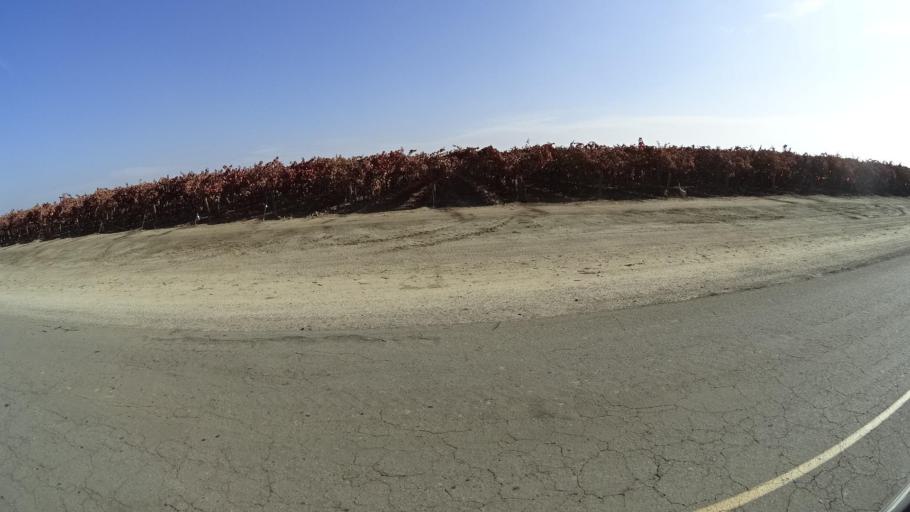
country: US
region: California
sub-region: Kern County
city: McFarland
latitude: 35.6499
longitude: -119.1691
